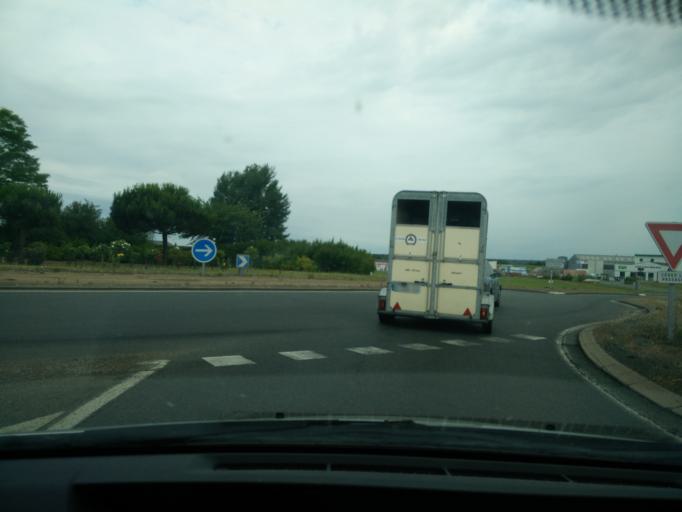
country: FR
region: Pays de la Loire
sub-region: Departement de Maine-et-Loire
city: Brissac-Quince
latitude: 47.3434
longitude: -0.4362
